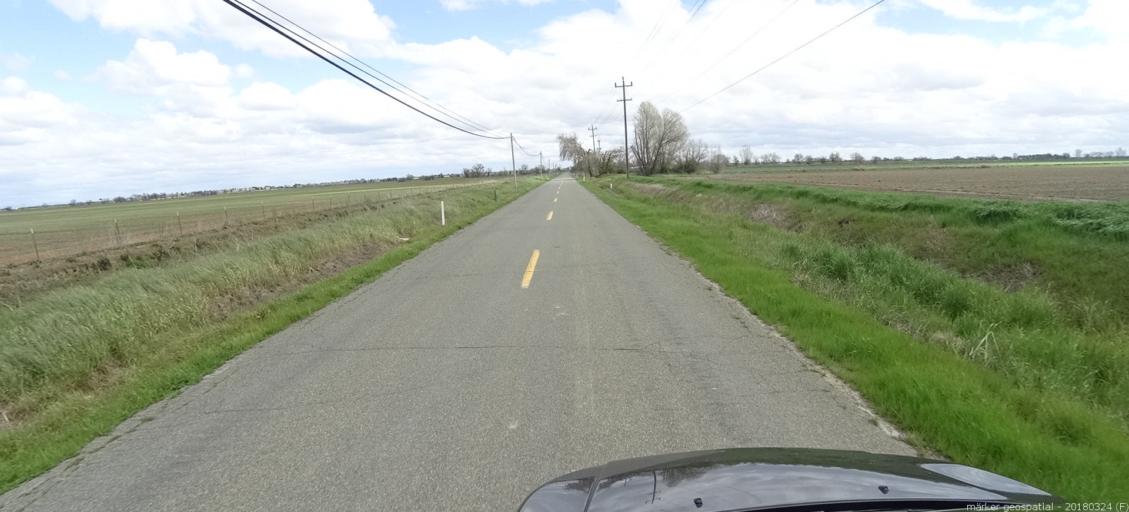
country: US
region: California
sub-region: Yolo County
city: West Sacramento
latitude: 38.6563
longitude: -121.5691
